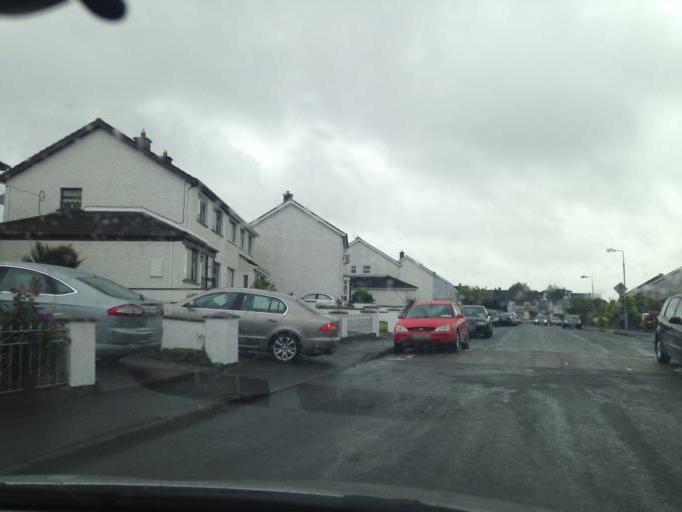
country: IE
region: Connaught
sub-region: County Galway
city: Gaillimh
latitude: 53.2887
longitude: -9.0322
